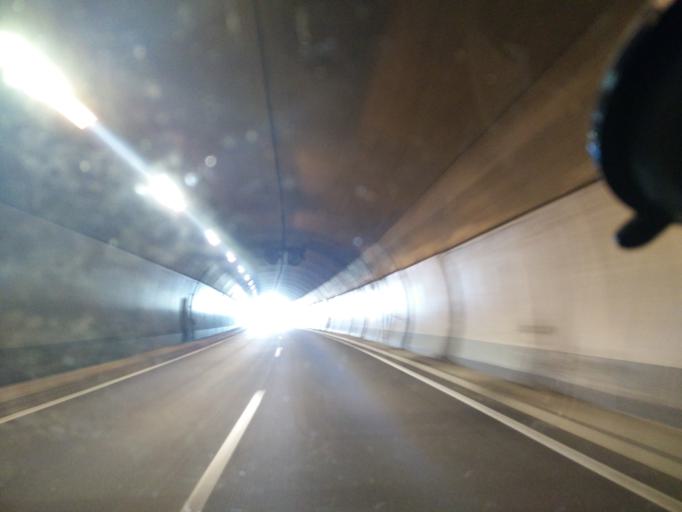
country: ES
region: Catalonia
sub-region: Provincia de Barcelona
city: Sant Cugat del Valles
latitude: 41.4509
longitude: 2.0696
